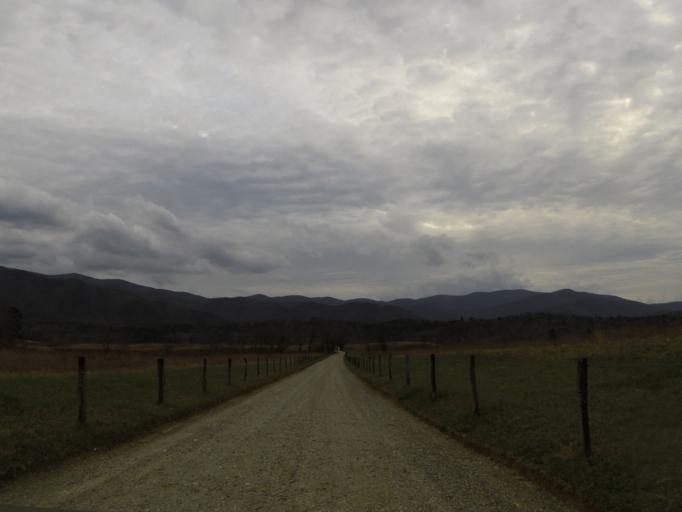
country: US
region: Tennessee
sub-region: Blount County
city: Wildwood
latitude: 35.6015
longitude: -83.8238
